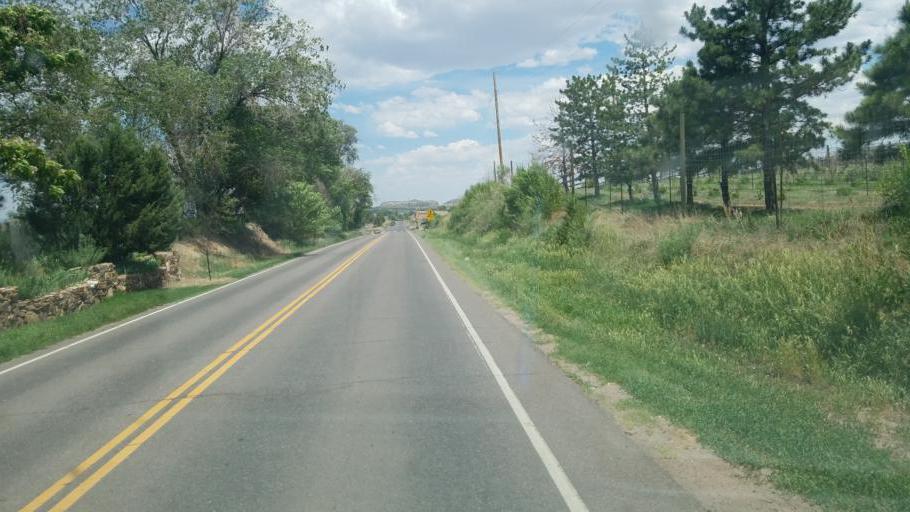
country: US
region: Colorado
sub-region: Fremont County
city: Lincoln Park
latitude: 38.4175
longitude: -105.1938
